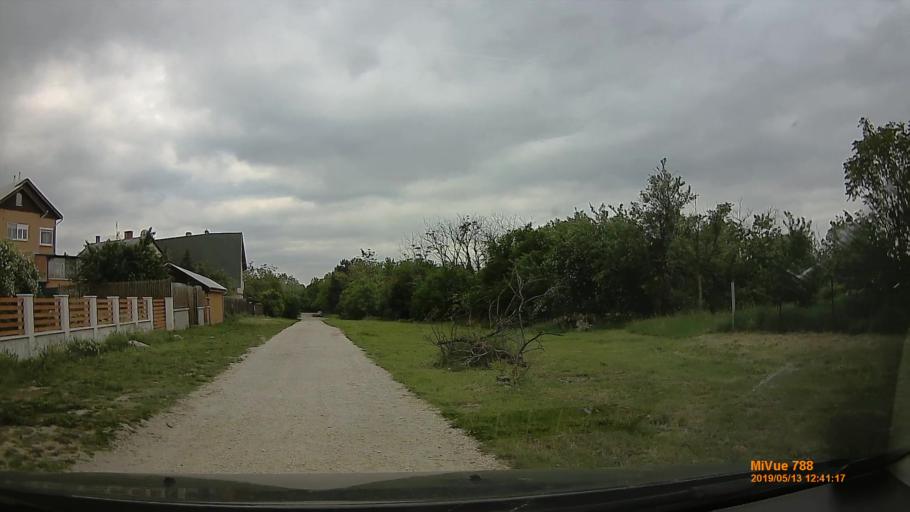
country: HU
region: Pest
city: Diosd
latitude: 47.4040
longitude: 18.9886
